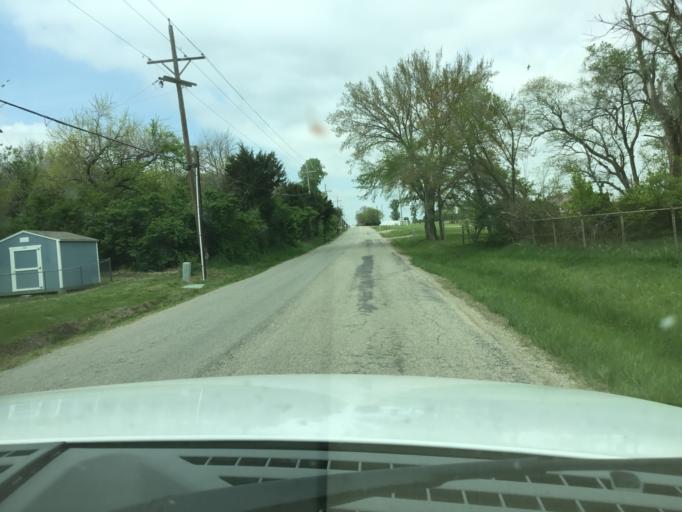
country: US
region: Kansas
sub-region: Shawnee County
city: Topeka
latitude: 39.0220
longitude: -95.5859
